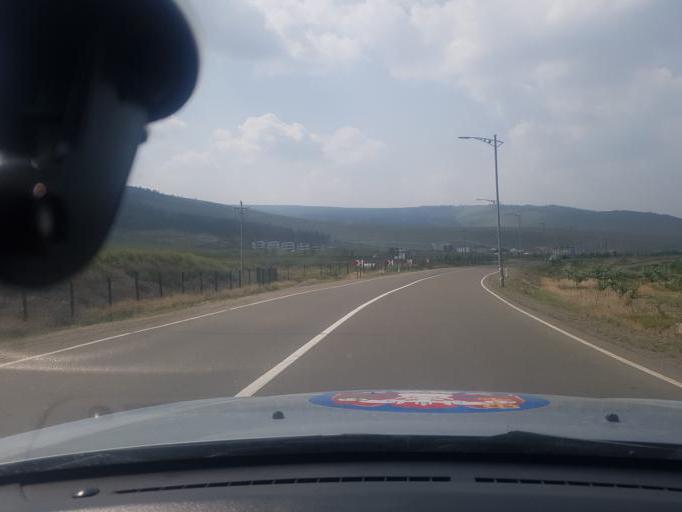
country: MN
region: Ulaanbaatar
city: Ulaanbaatar
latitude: 47.8881
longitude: 107.0262
